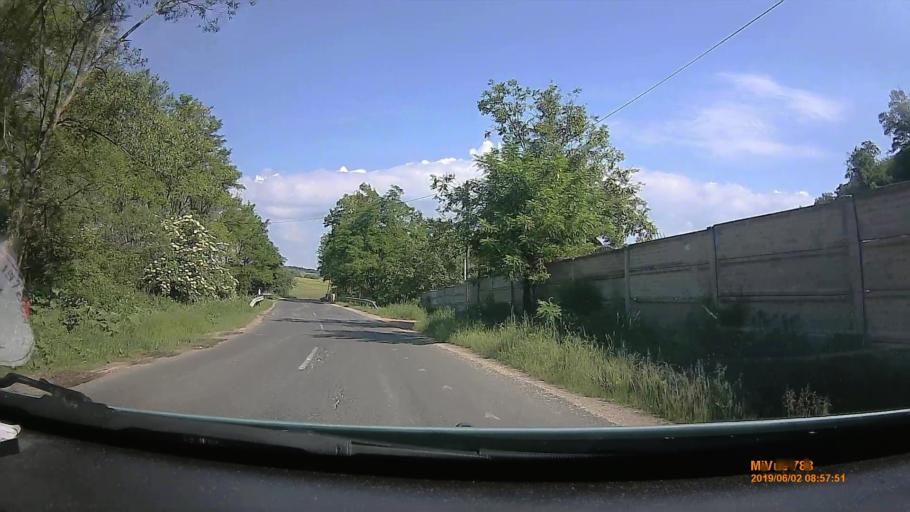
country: HU
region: Borsod-Abauj-Zemplen
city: Kazincbarcika
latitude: 48.1593
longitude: 20.6384
